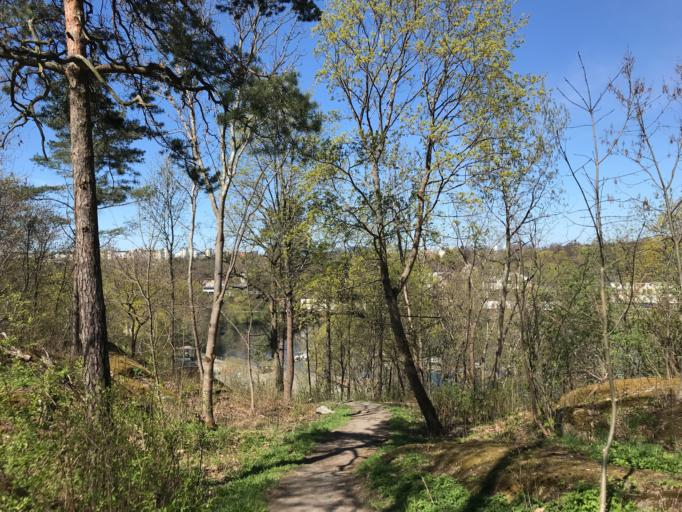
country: SE
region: Stockholm
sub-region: Solna Kommun
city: Solna
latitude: 59.3379
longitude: 18.0202
